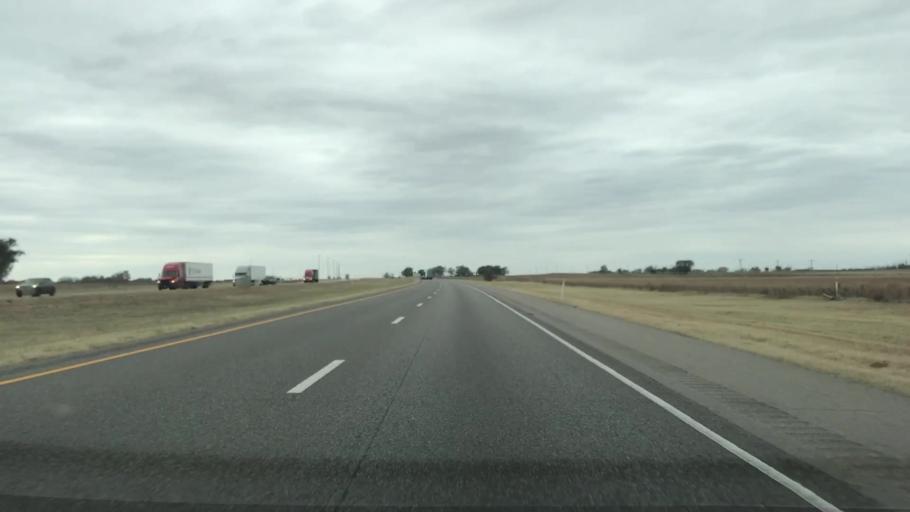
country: US
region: Oklahoma
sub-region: Beckham County
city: Erick
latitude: 35.2322
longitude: -99.9519
